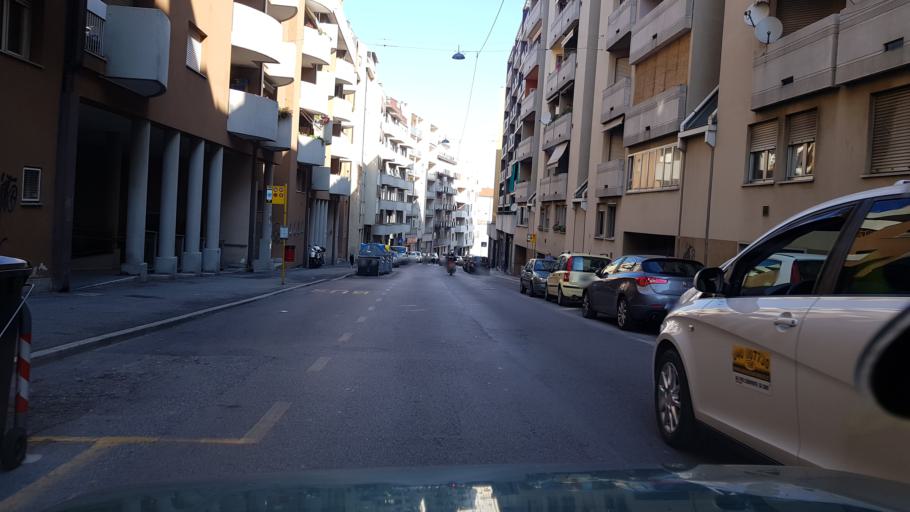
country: IT
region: Friuli Venezia Giulia
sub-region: Provincia di Trieste
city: Trieste
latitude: 45.6387
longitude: 13.7859
